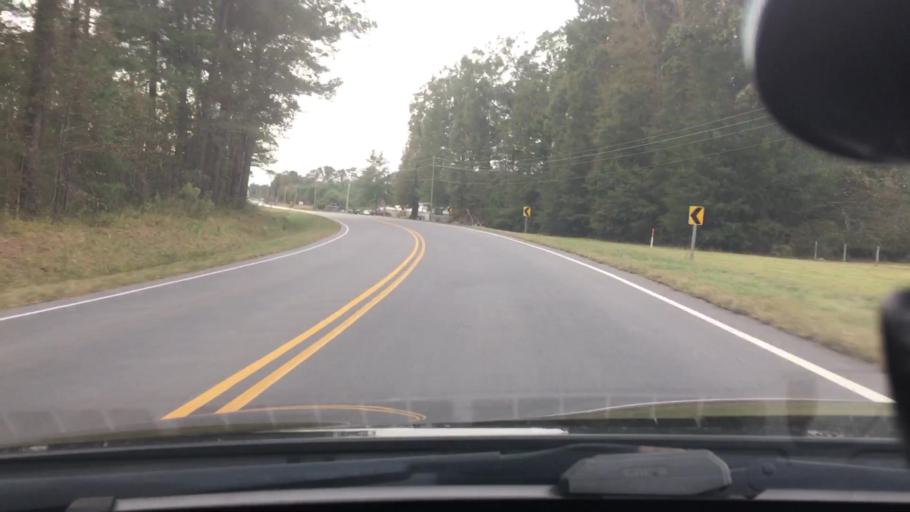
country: US
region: North Carolina
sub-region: Pitt County
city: Windsor
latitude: 35.4524
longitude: -77.2640
